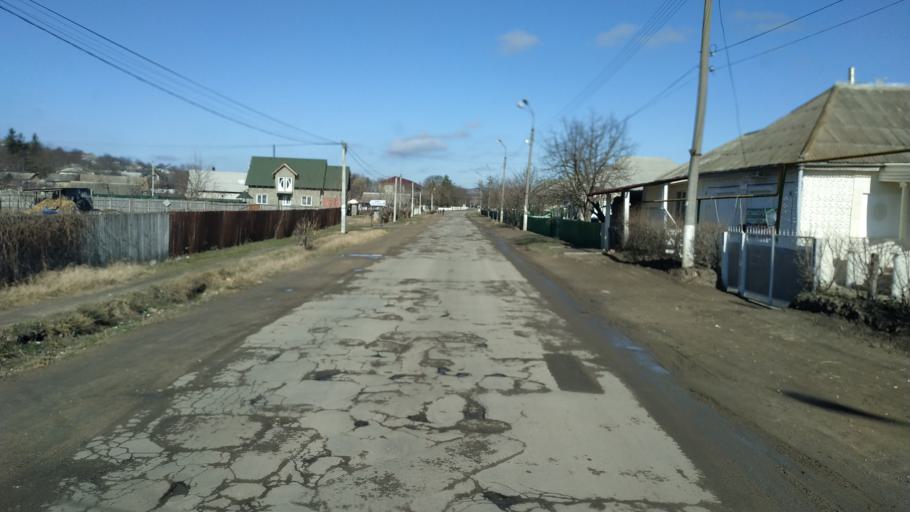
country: MD
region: Hincesti
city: Hincesti
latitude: 46.9582
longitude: 28.6047
